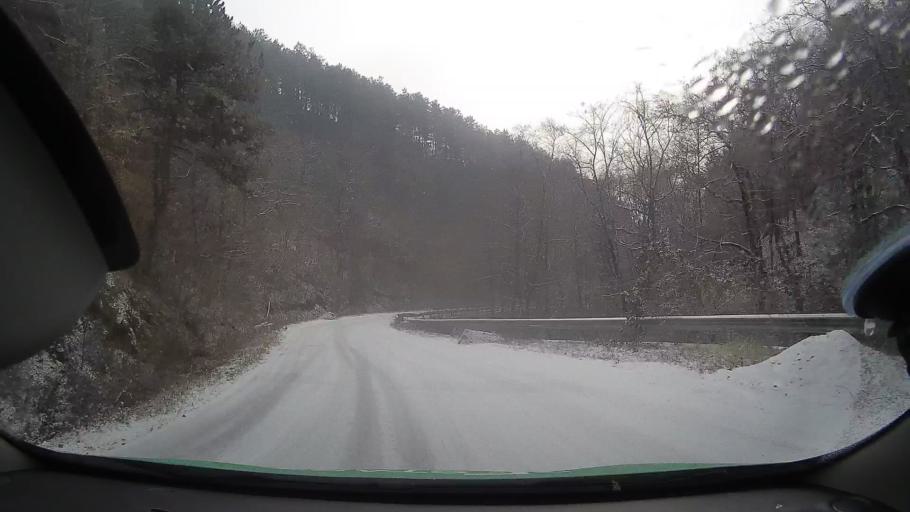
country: RO
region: Alba
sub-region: Comuna Livezile
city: Livezile
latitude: 46.3720
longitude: 23.5871
